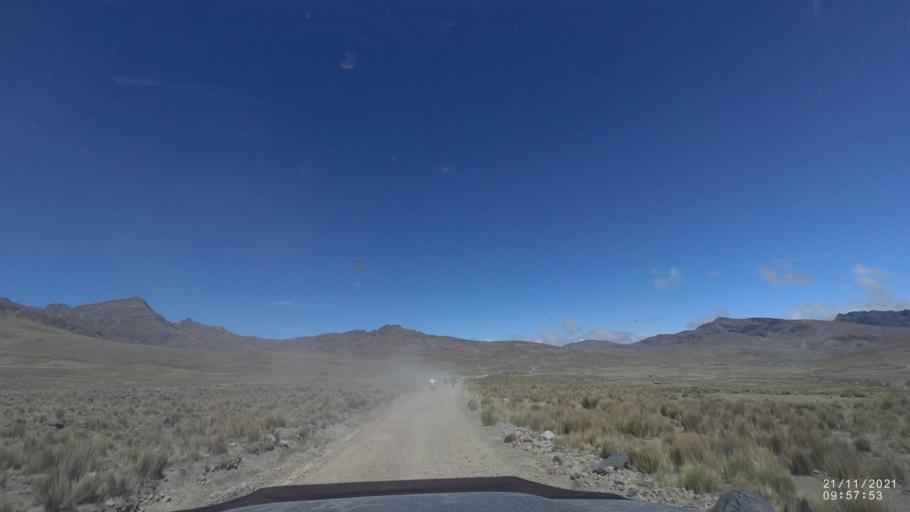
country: BO
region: Cochabamba
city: Cochabamba
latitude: -17.0379
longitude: -66.2737
